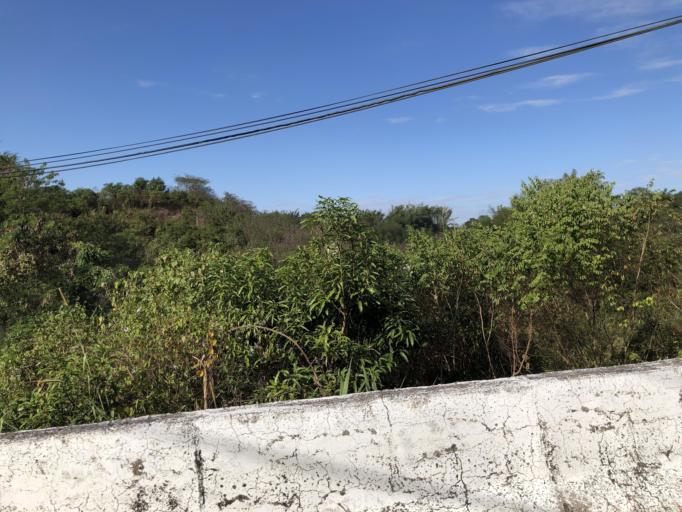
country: TW
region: Taiwan
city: Yujing
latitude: 23.0229
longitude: 120.3961
